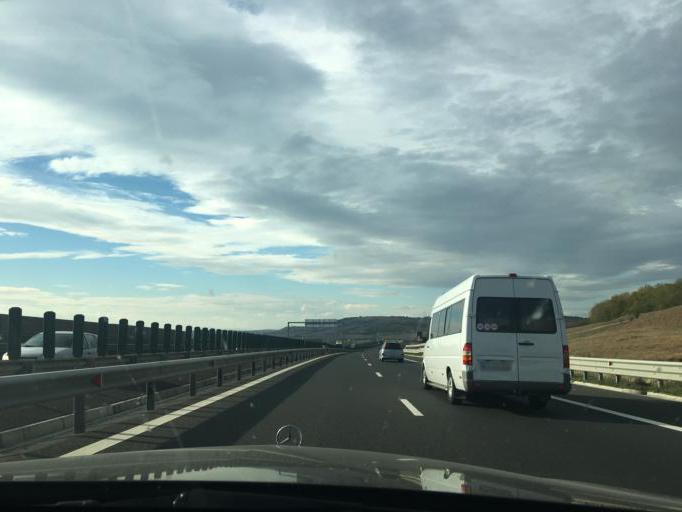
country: RO
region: Sibiu
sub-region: Comuna Apoldu de Jos
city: Apoldu de Jos
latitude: 45.8794
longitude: 23.8606
